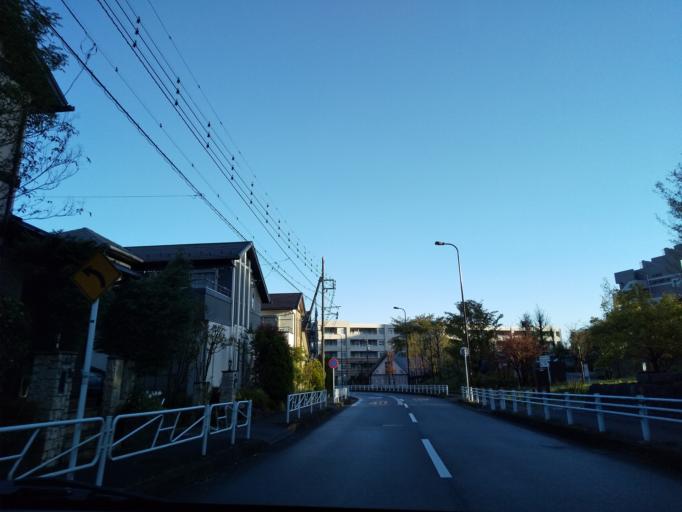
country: JP
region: Tokyo
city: Hachioji
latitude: 35.6163
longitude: 139.3678
